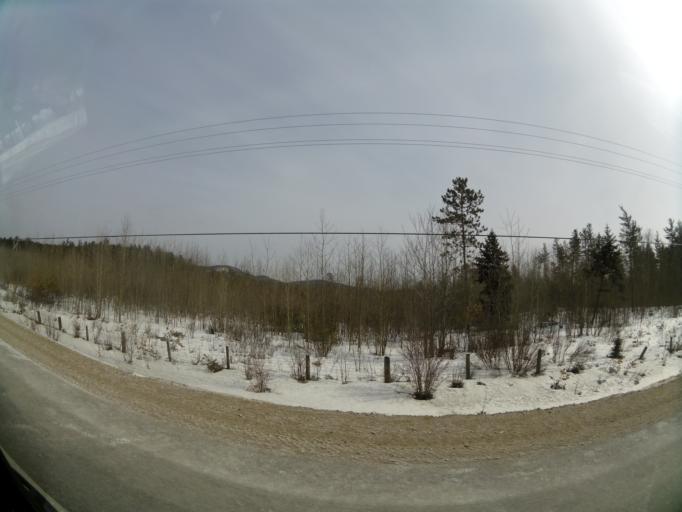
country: CA
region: Quebec
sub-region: Outaouais
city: Maniwaki
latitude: 46.1225
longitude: -75.6377
